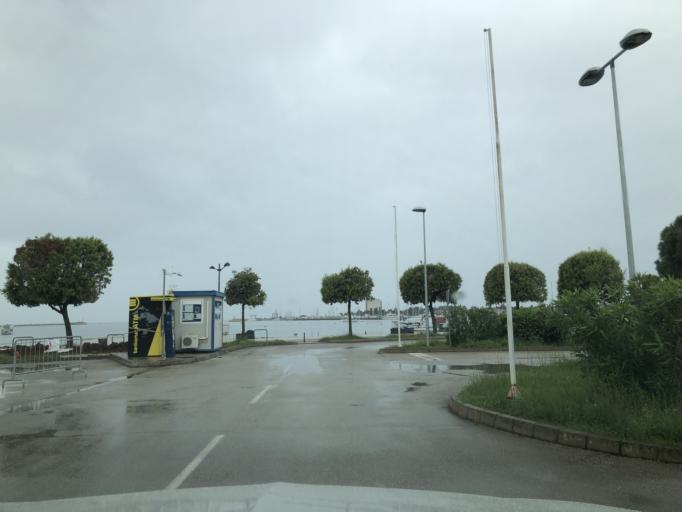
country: HR
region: Istarska
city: Umag
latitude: 45.4350
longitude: 13.5234
